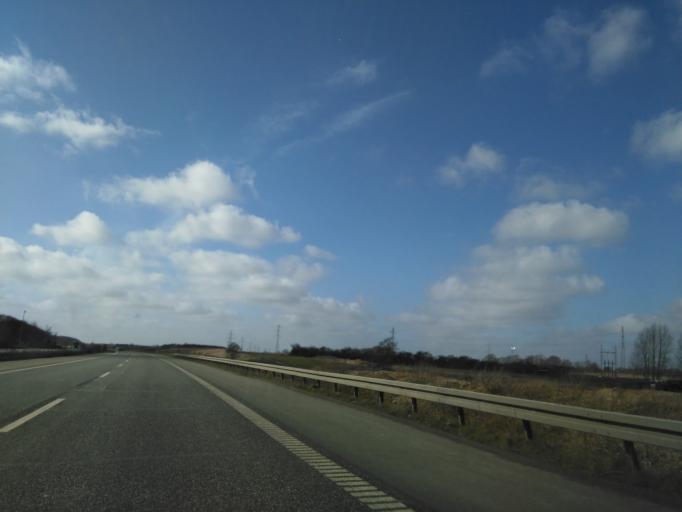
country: DK
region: Zealand
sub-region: Koge Kommune
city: Ejby
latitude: 55.4787
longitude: 12.0988
